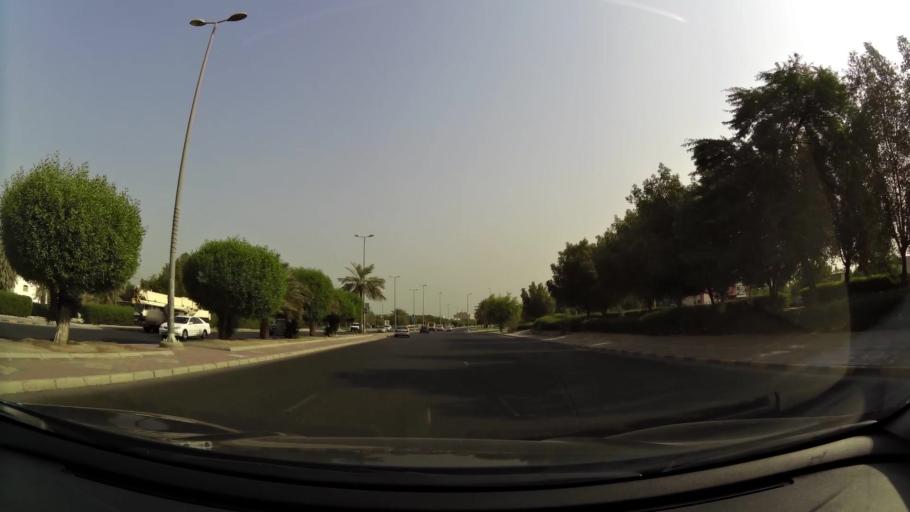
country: KW
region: Mubarak al Kabir
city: Sabah as Salim
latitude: 29.2504
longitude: 48.0664
